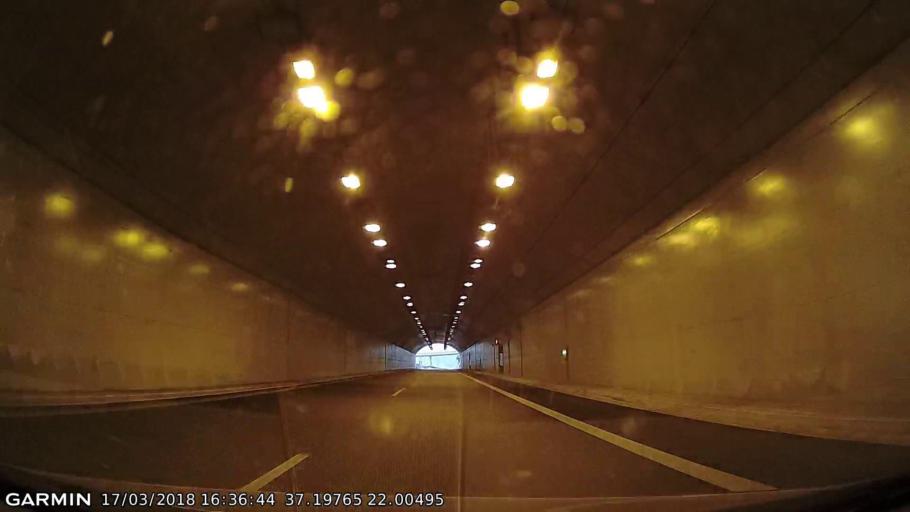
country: GR
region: Peloponnese
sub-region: Nomos Messinias
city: Meligalas
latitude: 37.1983
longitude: 22.0044
